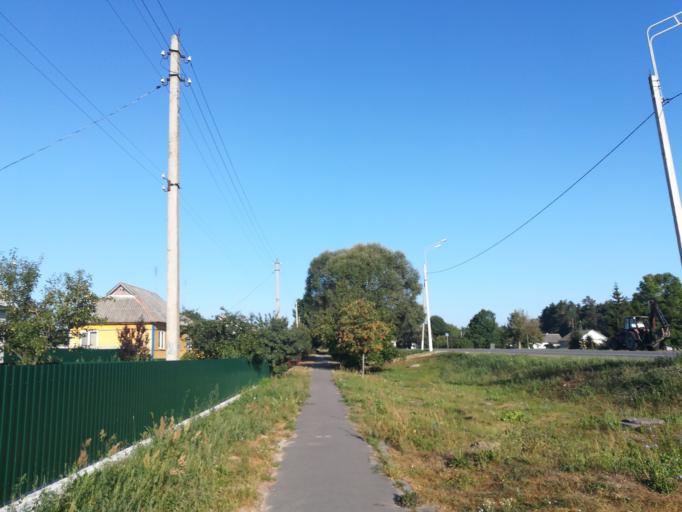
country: RU
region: Brjansk
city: Karachev
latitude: 53.1280
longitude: 34.9378
